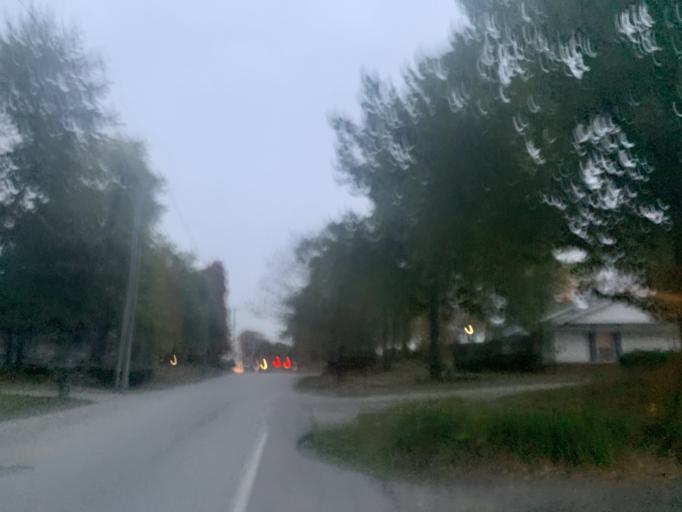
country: US
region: Kentucky
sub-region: Jefferson County
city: Shively
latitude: 38.2149
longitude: -85.7980
